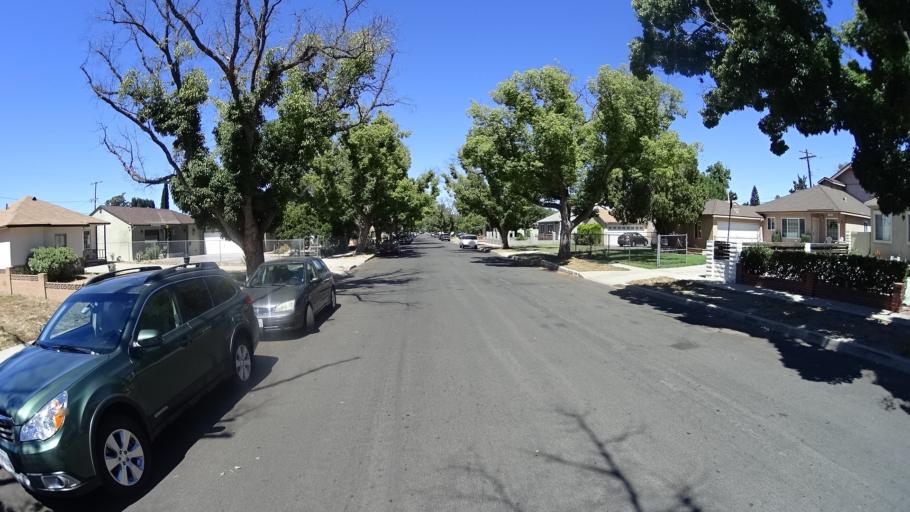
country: US
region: California
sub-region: Los Angeles County
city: San Fernando
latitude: 34.2509
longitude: -118.4546
